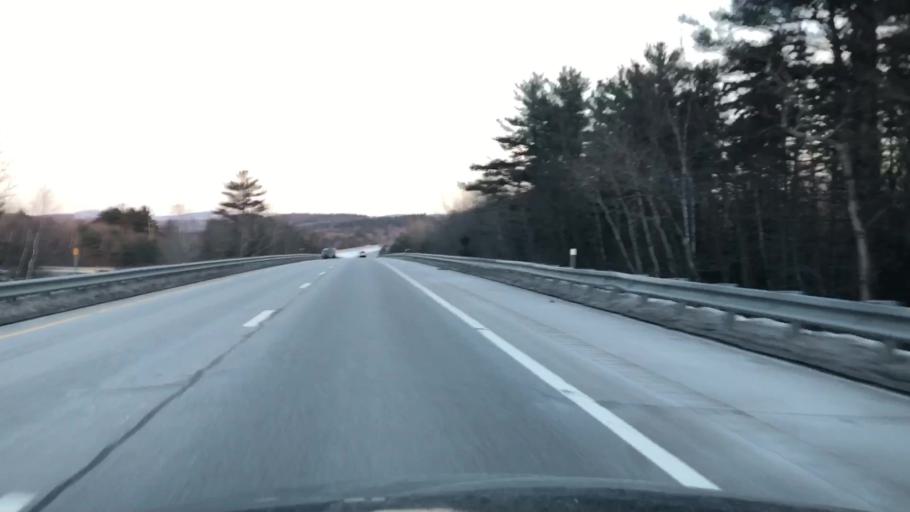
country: US
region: New Hampshire
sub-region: Merrimack County
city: New London
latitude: 43.4007
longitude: -72.0154
